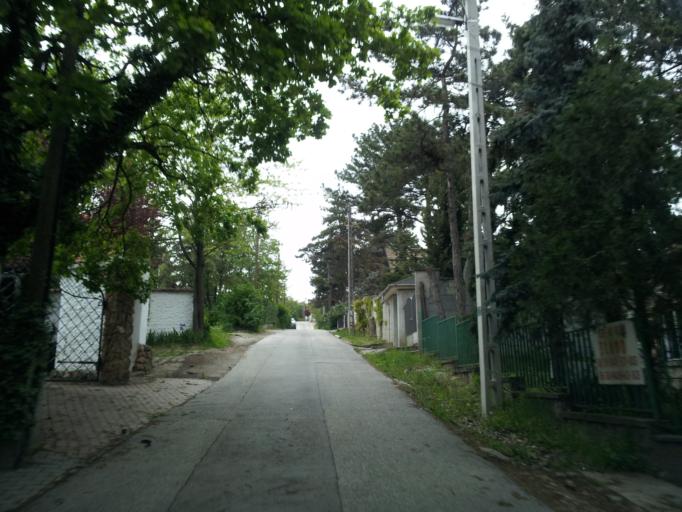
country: HU
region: Pest
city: Erd
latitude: 47.4007
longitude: 18.9293
